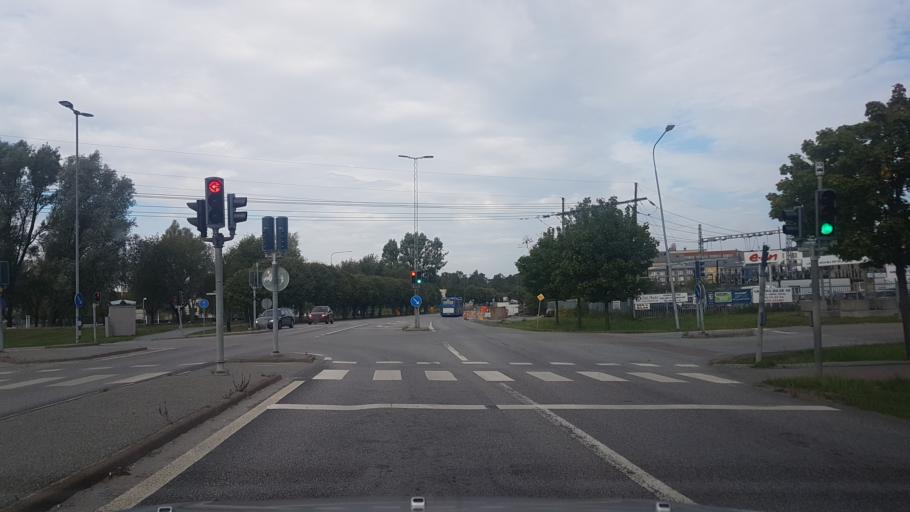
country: SE
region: Stockholm
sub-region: Jarfalla Kommun
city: Jakobsberg
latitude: 59.4146
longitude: 17.8287
